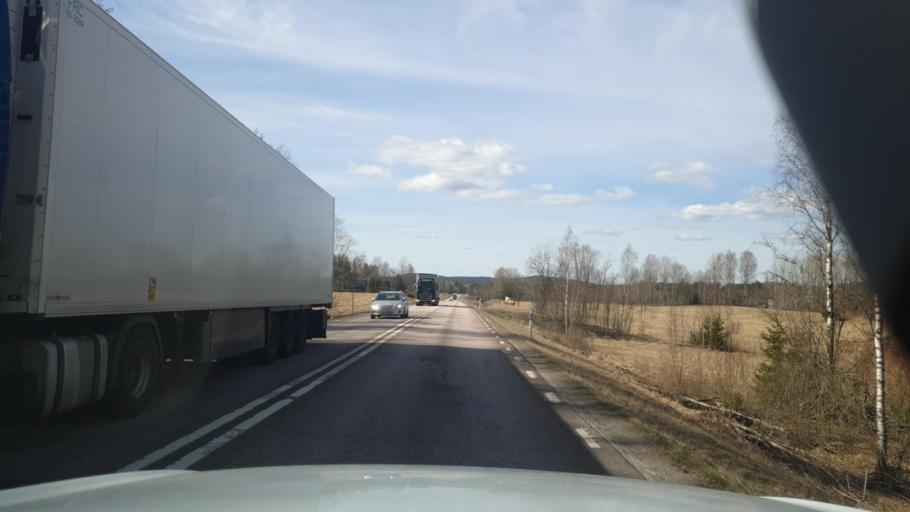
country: SE
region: Vaermland
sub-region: Karlstads Kommun
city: Edsvalla
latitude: 59.5494
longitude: 13.0582
